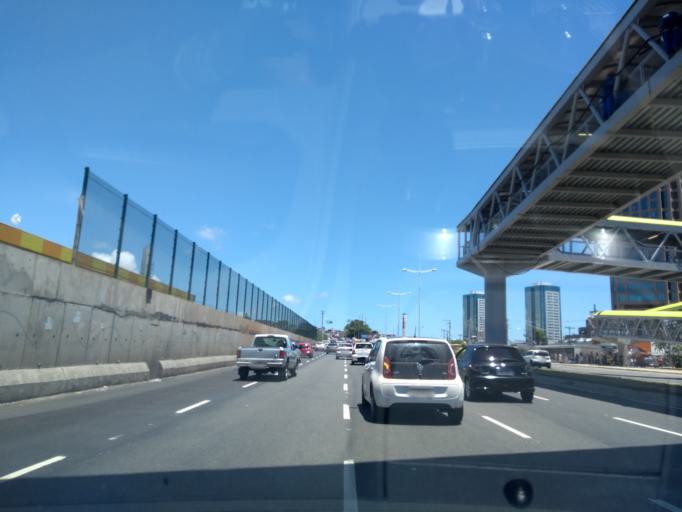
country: BR
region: Bahia
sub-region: Salvador
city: Salvador
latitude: -12.9792
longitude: -38.4637
